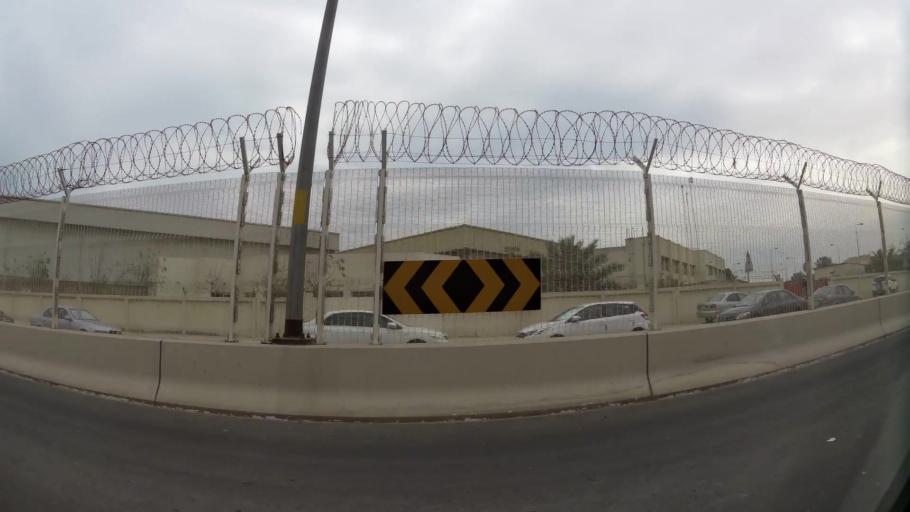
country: BH
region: Northern
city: Sitrah
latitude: 26.1838
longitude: 50.6096
